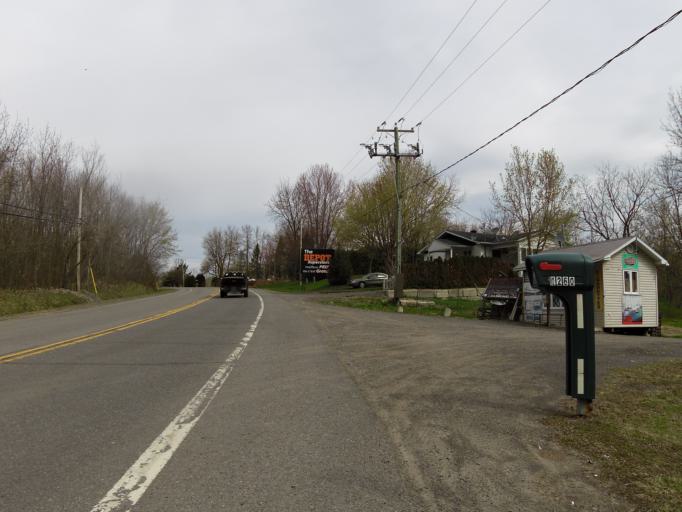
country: CA
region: Quebec
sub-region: Monteregie
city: Hudson
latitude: 45.4924
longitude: -74.1325
